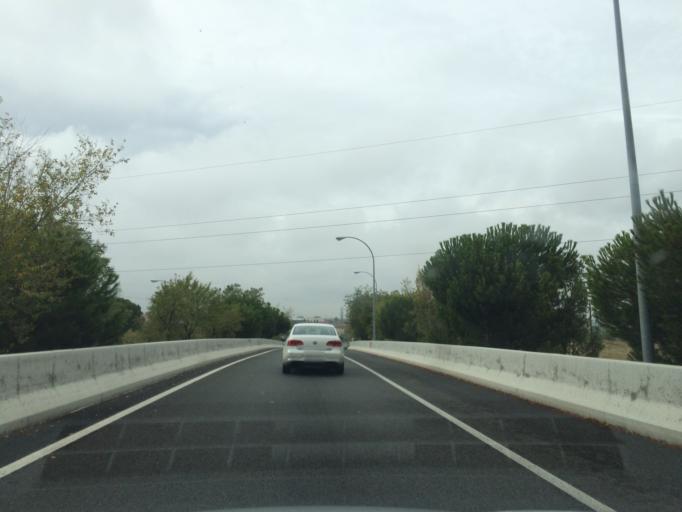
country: ES
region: Madrid
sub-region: Provincia de Madrid
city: Las Tablas
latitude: 40.5204
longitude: -3.6891
